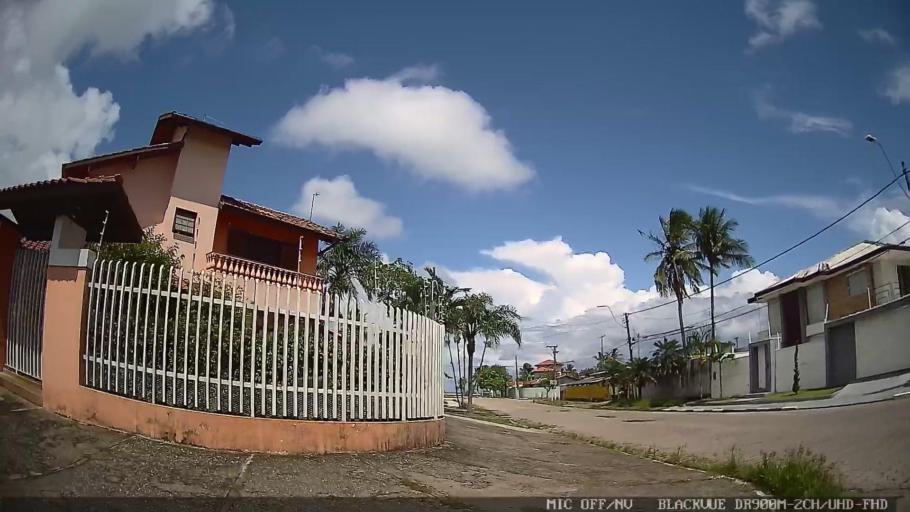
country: BR
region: Sao Paulo
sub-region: Caraguatatuba
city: Caraguatatuba
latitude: -23.6343
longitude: -45.4216
